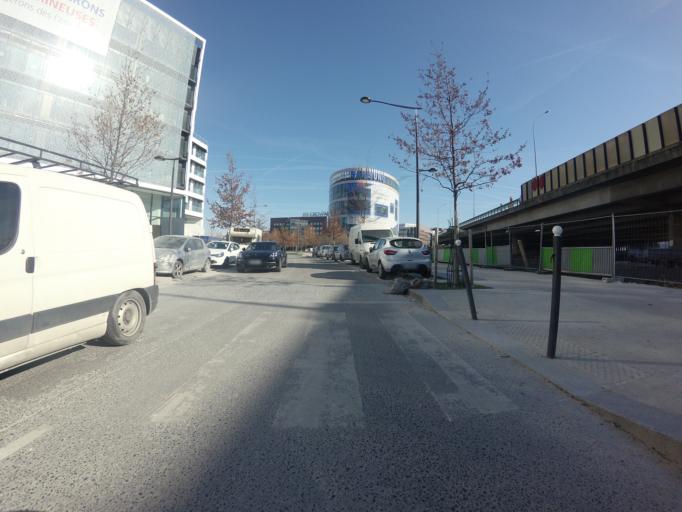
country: FR
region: Ile-de-France
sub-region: Departement des Hauts-de-Seine
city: Clichy
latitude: 48.9005
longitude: 2.3208
